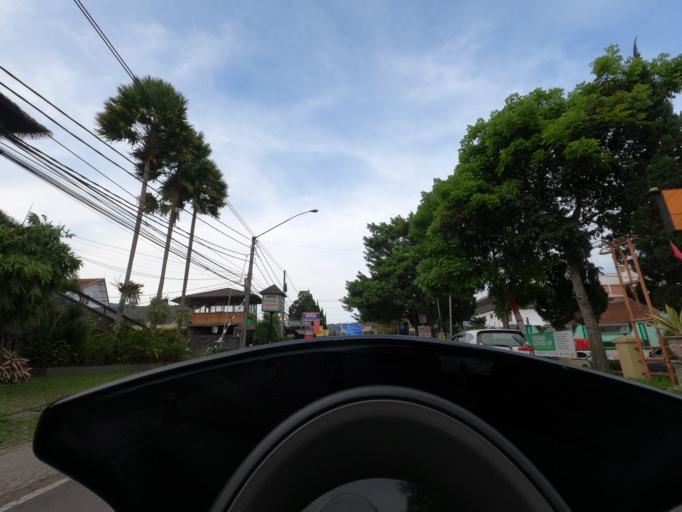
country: ID
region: West Java
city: Lembang
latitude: -6.8139
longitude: 107.6149
